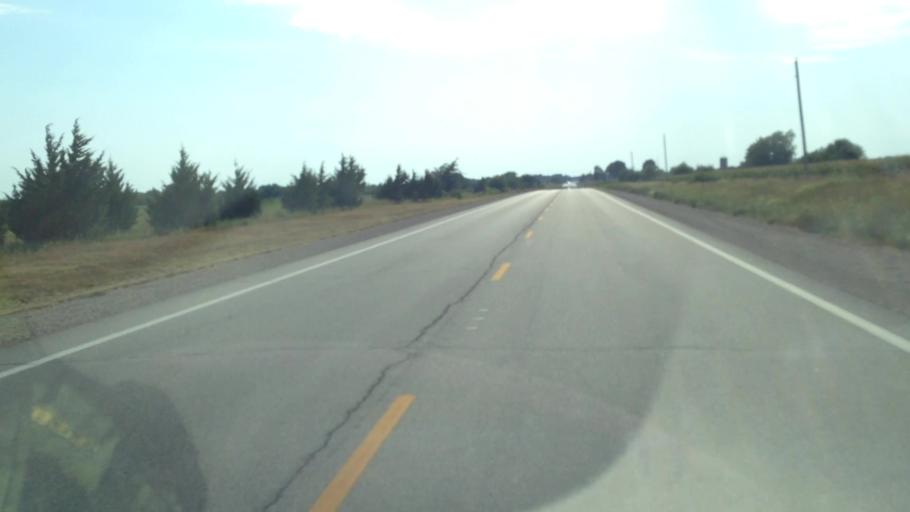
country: US
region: Kansas
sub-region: Anderson County
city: Garnett
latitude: 38.0816
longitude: -95.2171
